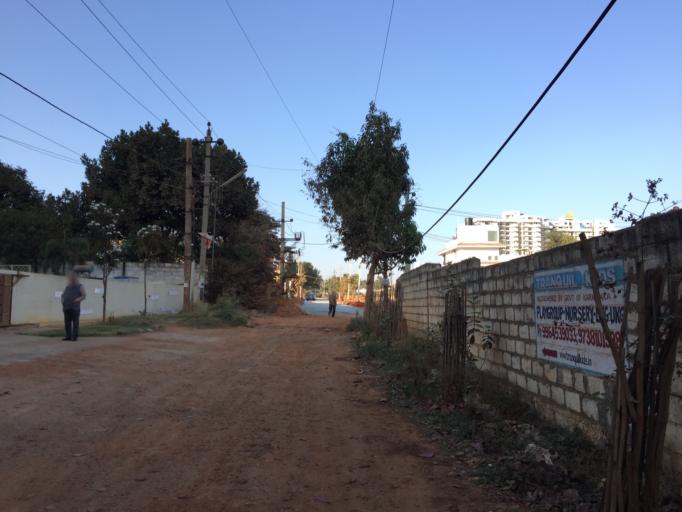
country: IN
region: Karnataka
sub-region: Bangalore Urban
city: Yelahanka
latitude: 13.0582
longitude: 77.6303
